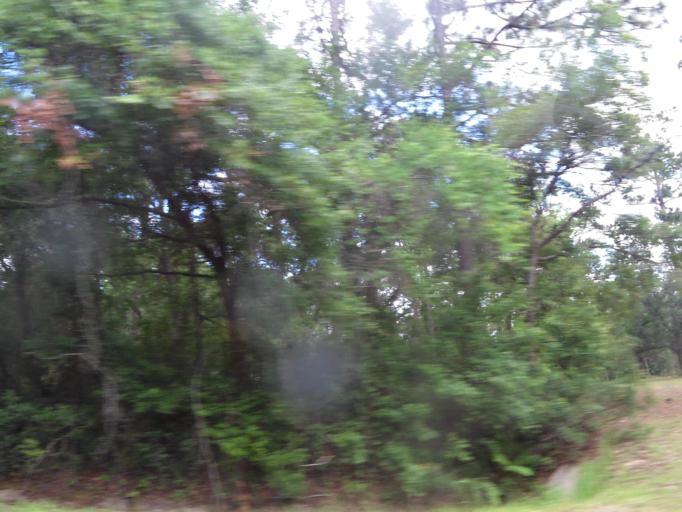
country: US
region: Florida
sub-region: Clay County
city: Green Cove Springs
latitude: 29.9183
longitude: -81.7681
